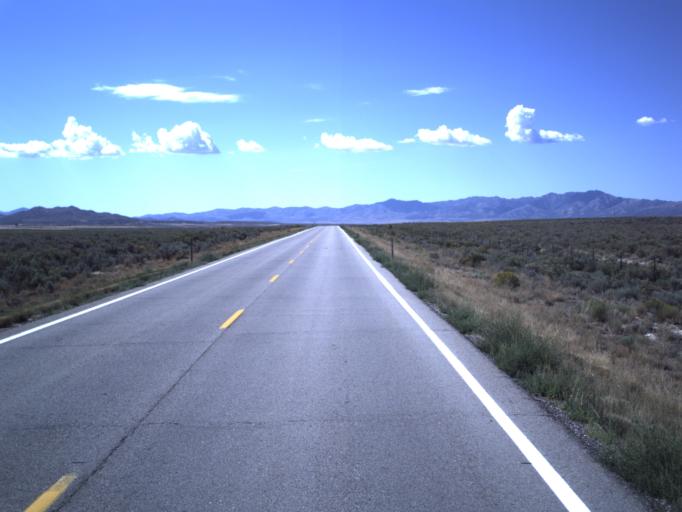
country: US
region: Utah
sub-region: Tooele County
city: Tooele
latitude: 40.2300
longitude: -112.4035
